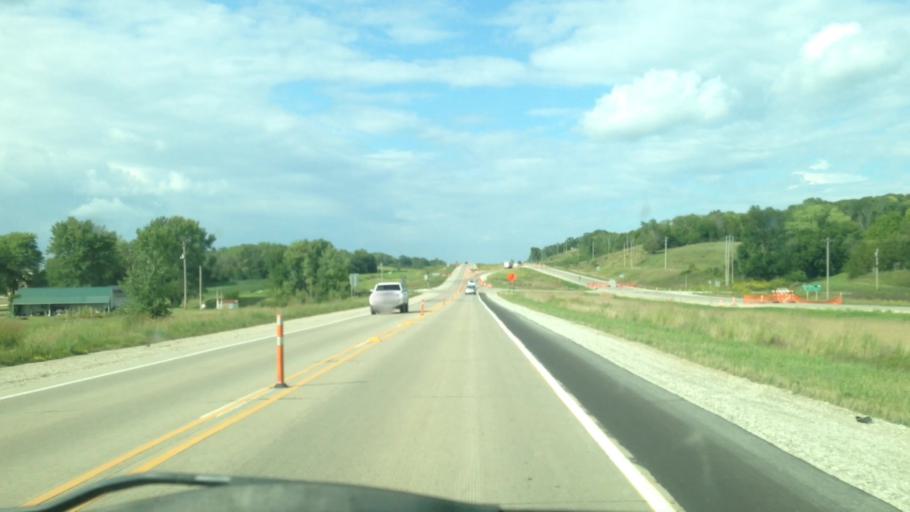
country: US
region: Iowa
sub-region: Henry County
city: Mount Pleasant
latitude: 40.8996
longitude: -91.5550
